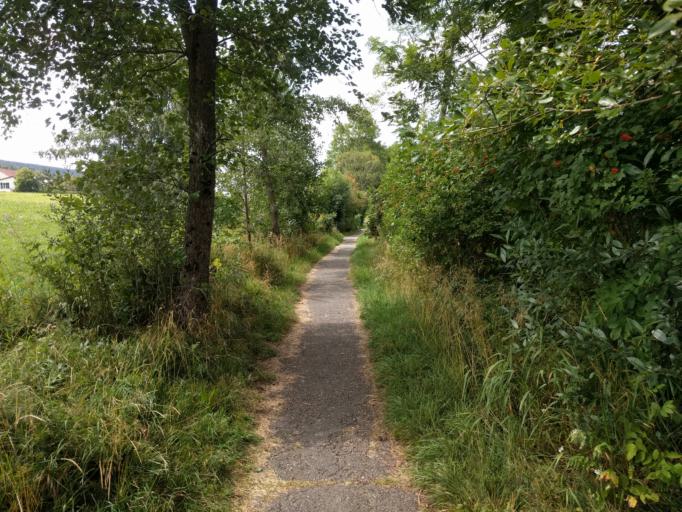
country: CH
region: Vaud
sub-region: Jura-Nord vaudois District
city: Le Chenit
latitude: 46.6190
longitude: 6.2632
